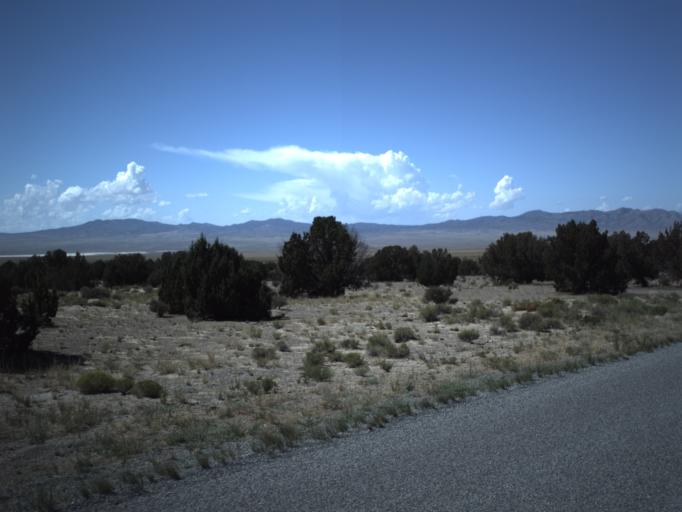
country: US
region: Utah
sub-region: Beaver County
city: Milford
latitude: 39.0717
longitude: -113.7243
